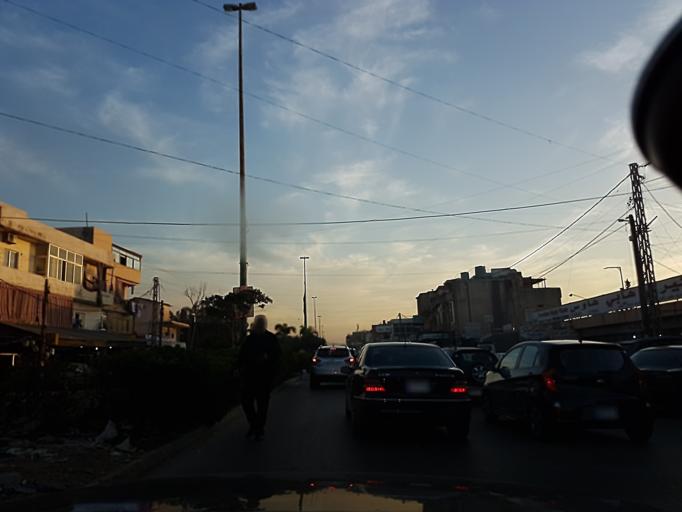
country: LB
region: Beyrouth
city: Beirut
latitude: 33.8393
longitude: 35.4847
